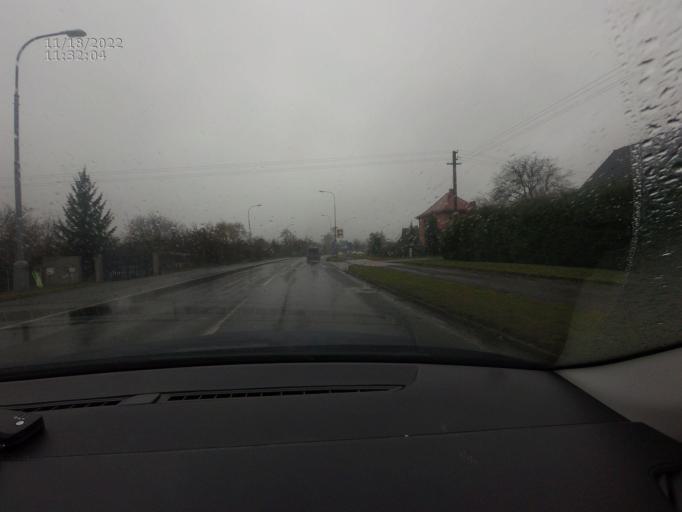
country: CZ
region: Plzensky
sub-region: Okres Rokycany
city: Rokycany
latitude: 49.7351
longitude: 13.5862
